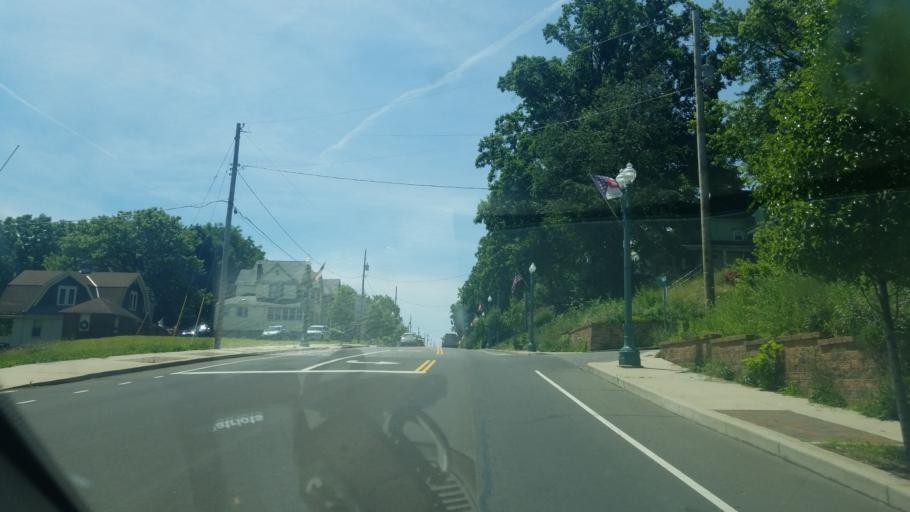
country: US
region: Ohio
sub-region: Stark County
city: Canton
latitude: 40.8088
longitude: -81.3577
